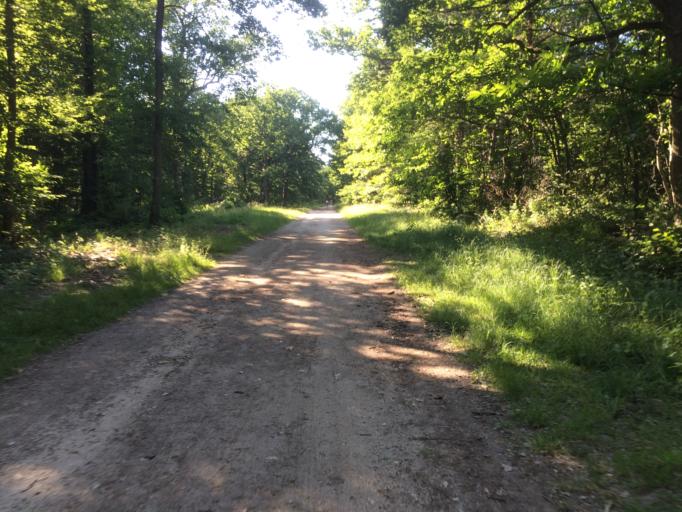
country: FR
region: Ile-de-France
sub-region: Departement du Val-de-Marne
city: Sucy-en-Brie
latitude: 48.7487
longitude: 2.5535
